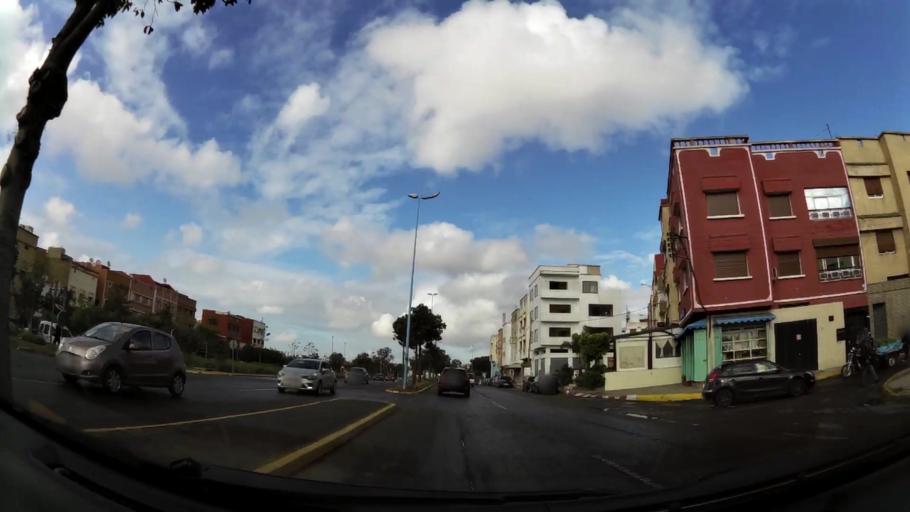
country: MA
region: Grand Casablanca
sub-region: Casablanca
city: Casablanca
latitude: 33.5487
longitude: -7.5890
